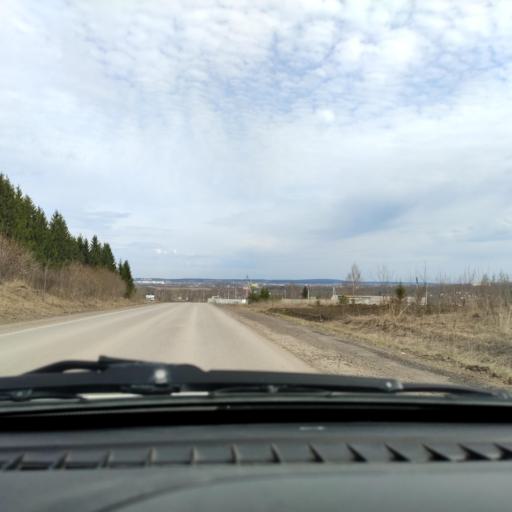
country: RU
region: Perm
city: Lobanovo
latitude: 57.8593
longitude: 56.2959
